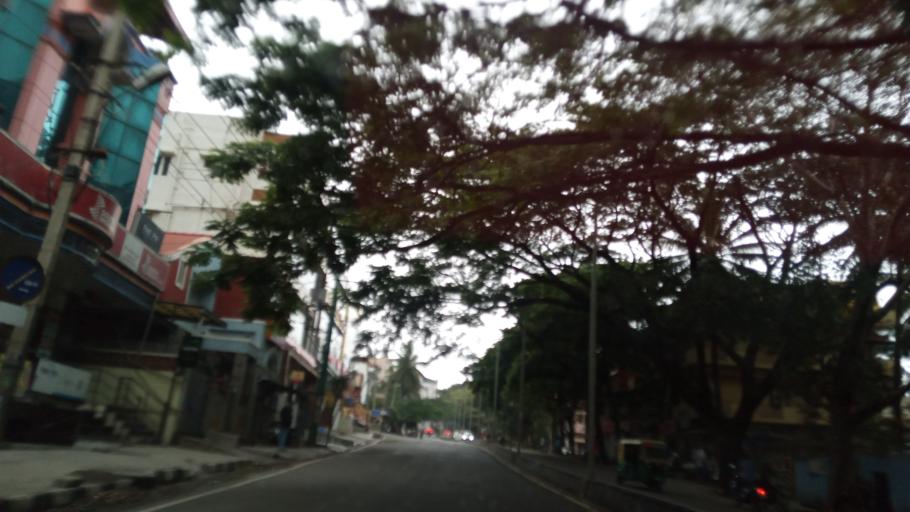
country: IN
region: Karnataka
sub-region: Bangalore Urban
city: Bangalore
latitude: 12.9236
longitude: 77.5605
